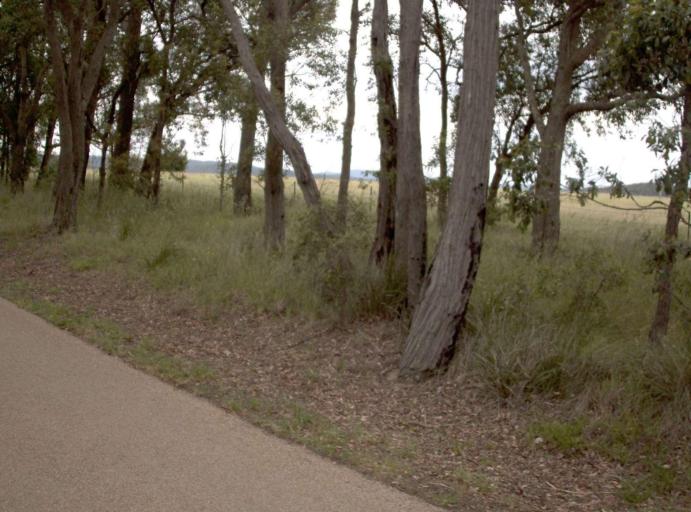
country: AU
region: Victoria
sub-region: East Gippsland
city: Bairnsdale
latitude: -37.7362
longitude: 147.5950
